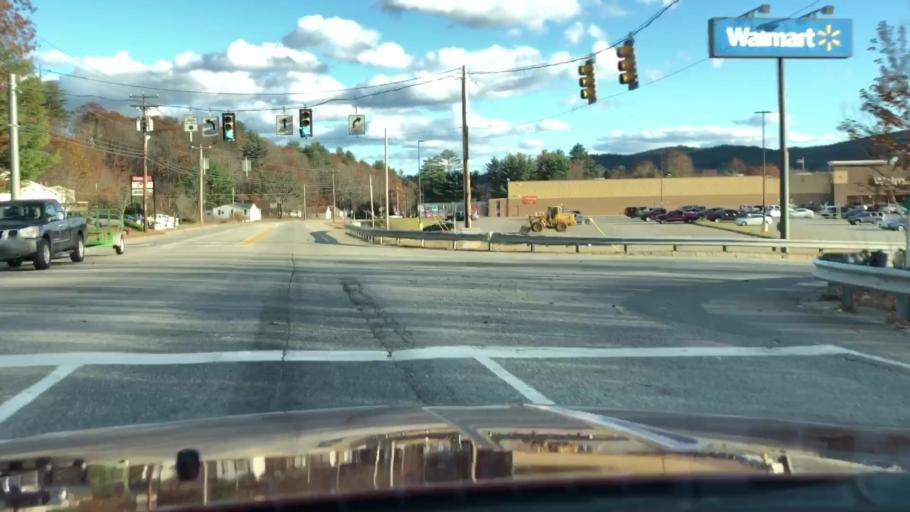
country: US
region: Maine
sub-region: Oxford County
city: Mexico
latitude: 44.5402
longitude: -70.5185
